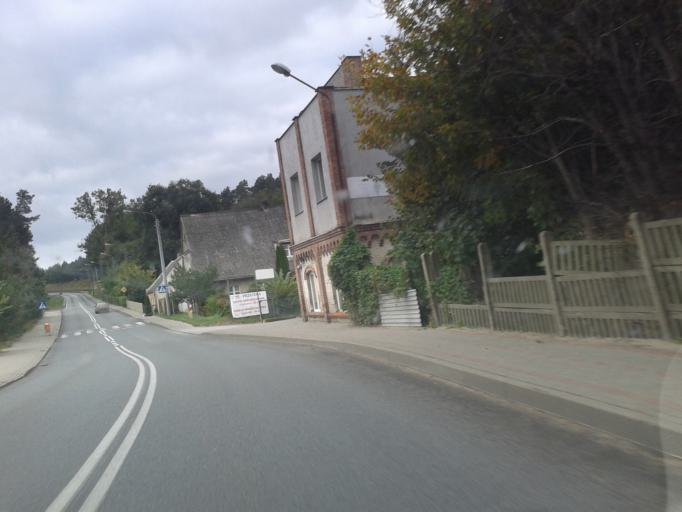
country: PL
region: Kujawsko-Pomorskie
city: Kamien Krajenski
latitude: 53.5359
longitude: 17.5224
